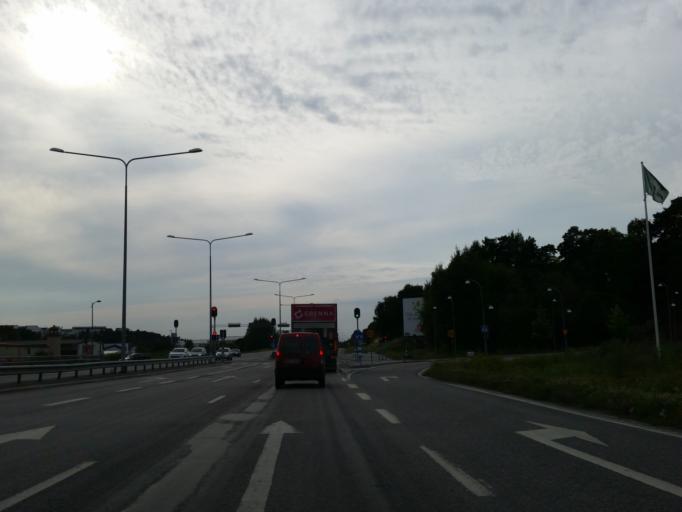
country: SE
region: Stockholm
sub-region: Sundbybergs Kommun
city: Sundbyberg
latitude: 59.3798
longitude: 17.9558
